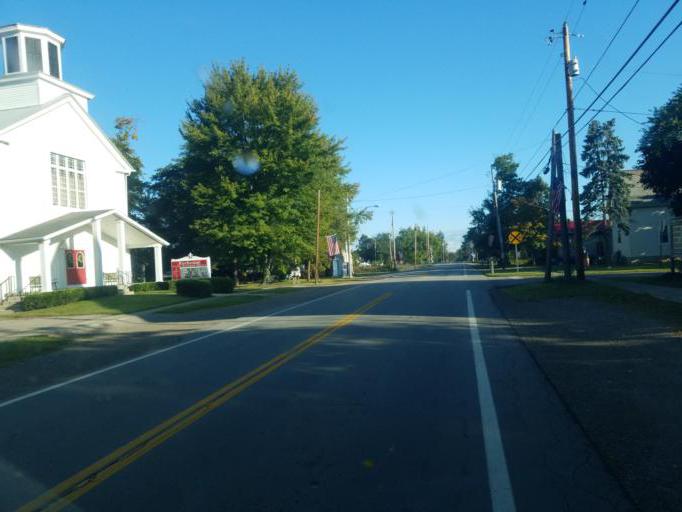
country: US
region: Ohio
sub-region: Lorain County
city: Wellington
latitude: 41.1244
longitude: -82.3042
